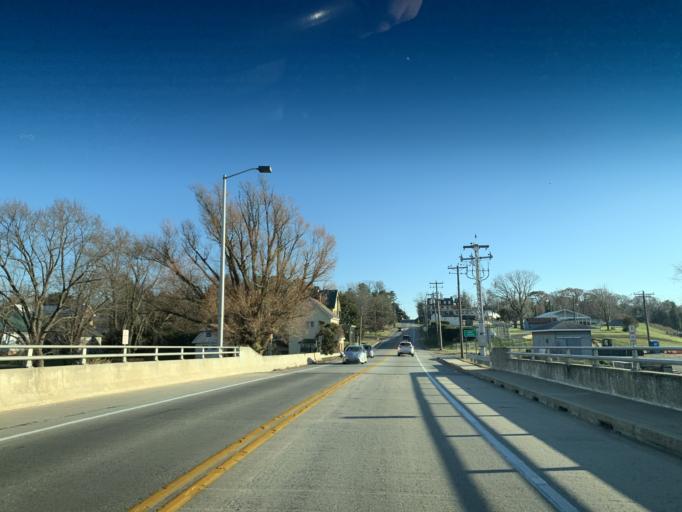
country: US
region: Delaware
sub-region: New Castle County
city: Middletown
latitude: 39.3638
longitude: -75.8817
